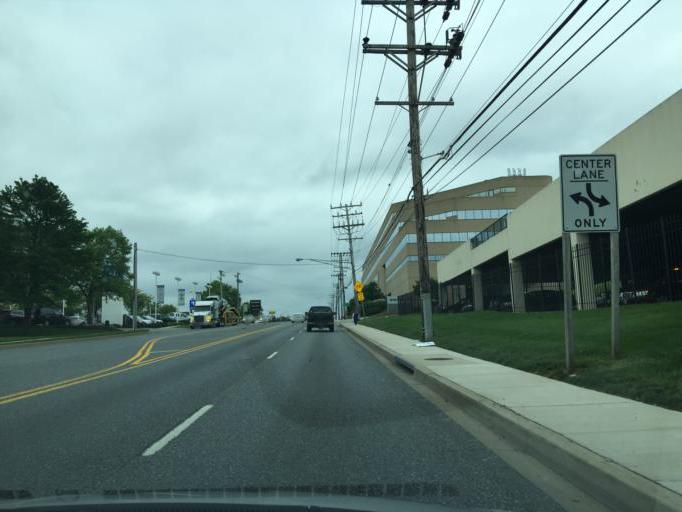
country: US
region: Maryland
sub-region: Baltimore County
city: Cockeysville
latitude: 39.4687
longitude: -76.6385
